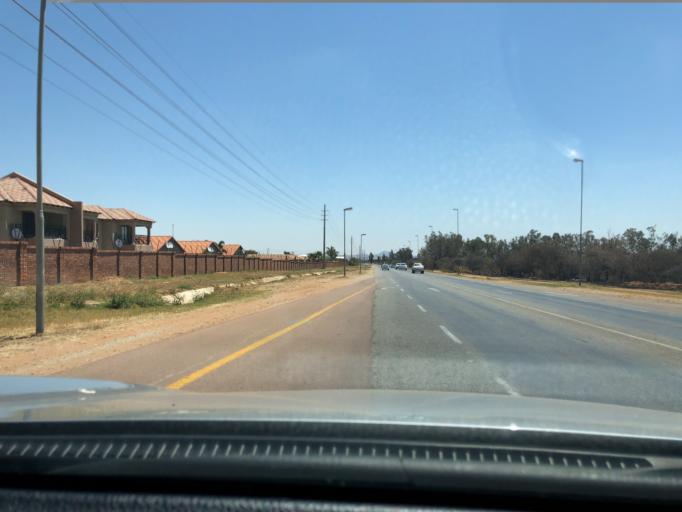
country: ZA
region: Limpopo
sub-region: Capricorn District Municipality
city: Polokwane
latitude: -23.8742
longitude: 29.4887
